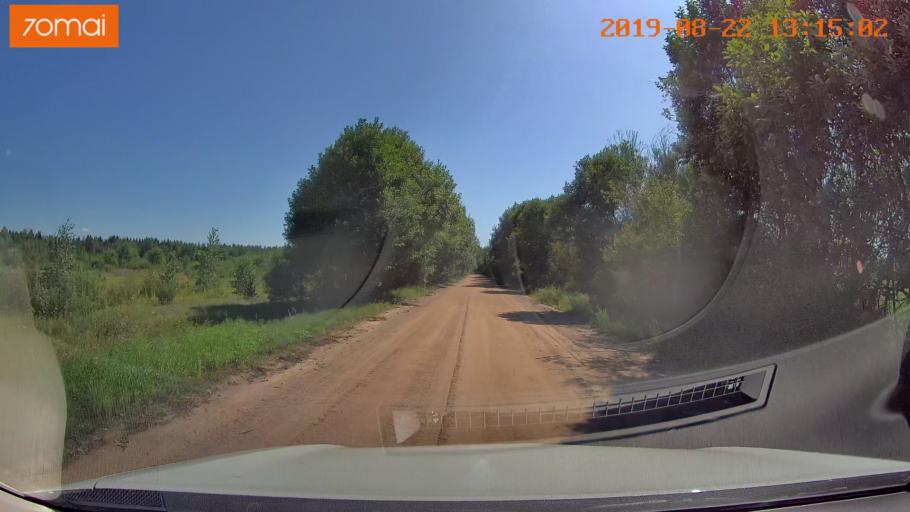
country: BY
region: Minsk
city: Prawdzinski
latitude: 53.2633
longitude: 27.8925
